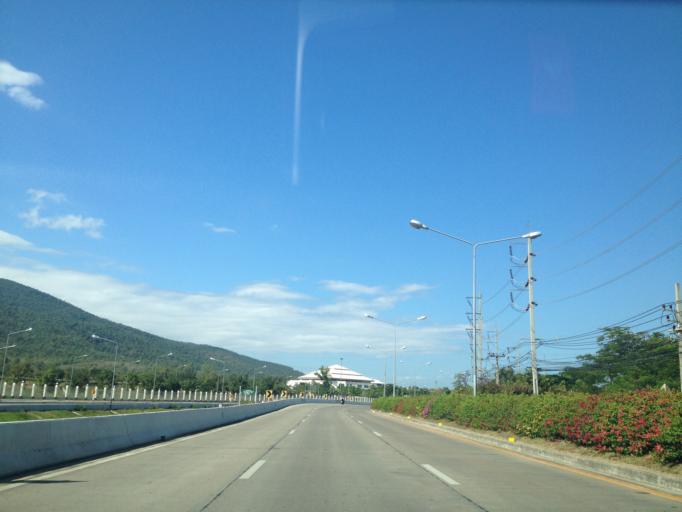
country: TH
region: Chiang Mai
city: Chiang Mai
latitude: 18.8276
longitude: 98.9647
